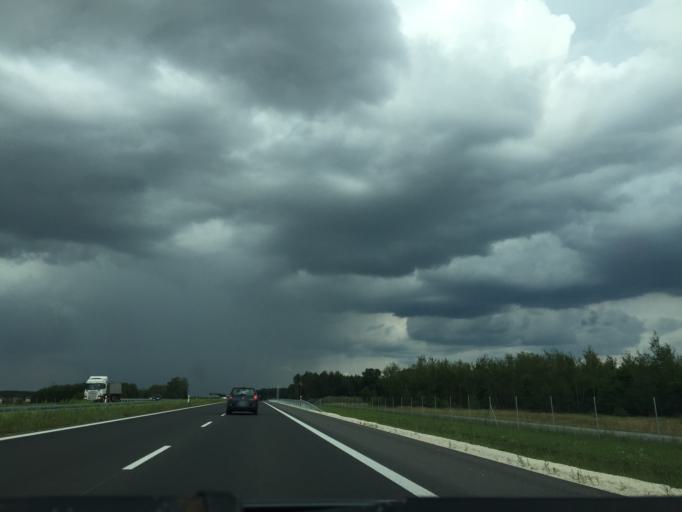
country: PL
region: Masovian Voivodeship
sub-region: Powiat szydlowiecki
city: Oronsko
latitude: 51.2826
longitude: 20.9677
